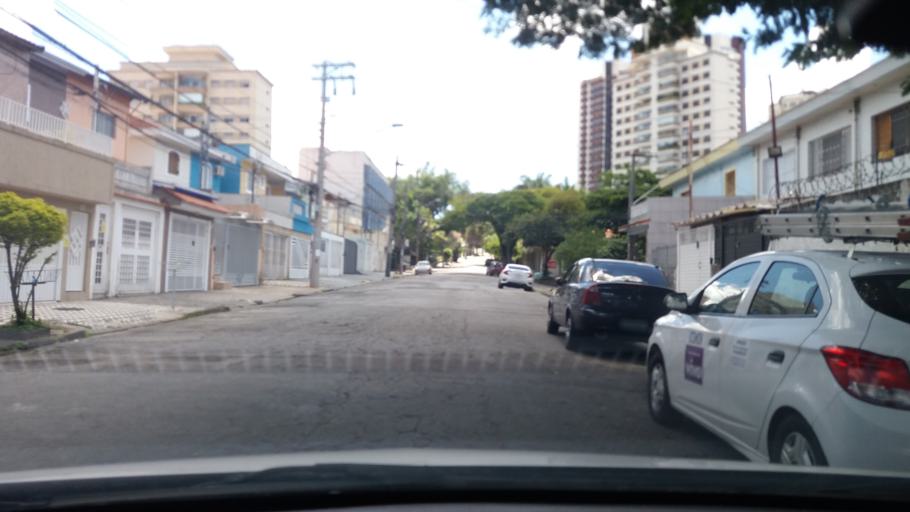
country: BR
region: Sao Paulo
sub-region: Sao Paulo
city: Sao Paulo
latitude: -23.4813
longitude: -46.6189
